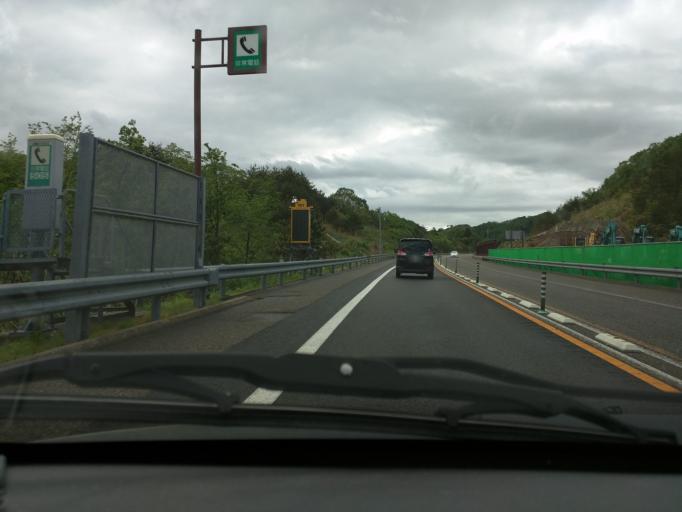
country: JP
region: Niigata
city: Joetsu
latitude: 37.1157
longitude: 138.2177
